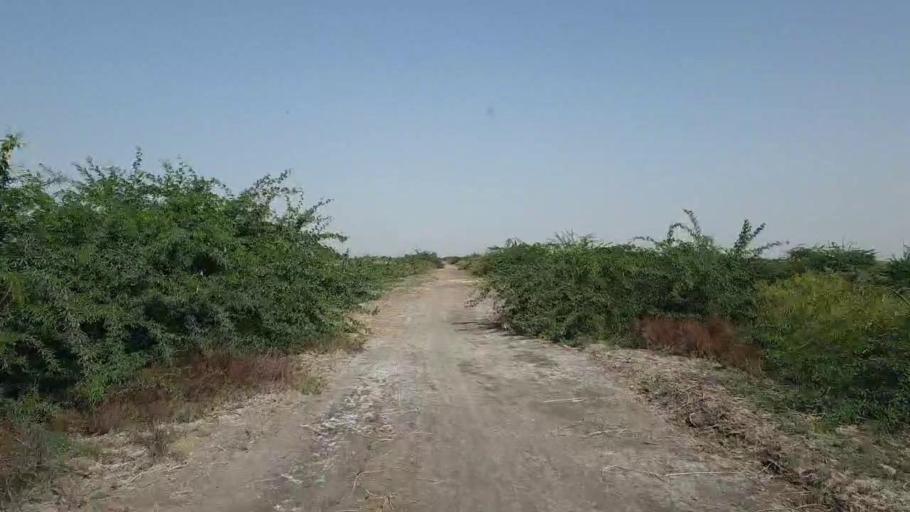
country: PK
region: Sindh
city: Tando Bago
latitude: 24.7139
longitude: 69.0720
